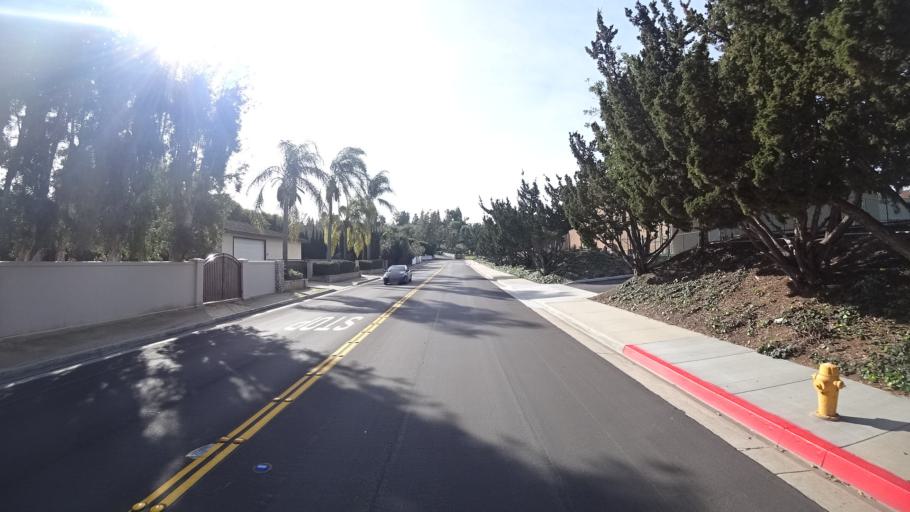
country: US
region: California
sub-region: Orange County
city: Yorba Linda
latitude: 33.8588
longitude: -117.7664
